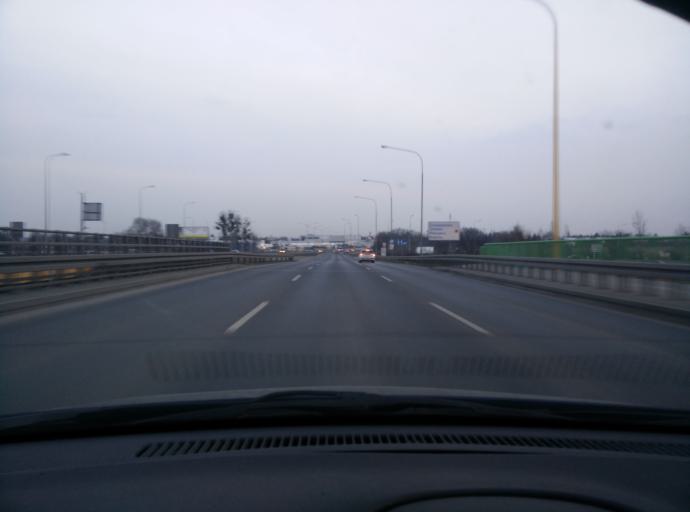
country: PL
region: Greater Poland Voivodeship
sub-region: Poznan
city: Poznan
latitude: 52.3708
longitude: 16.9885
